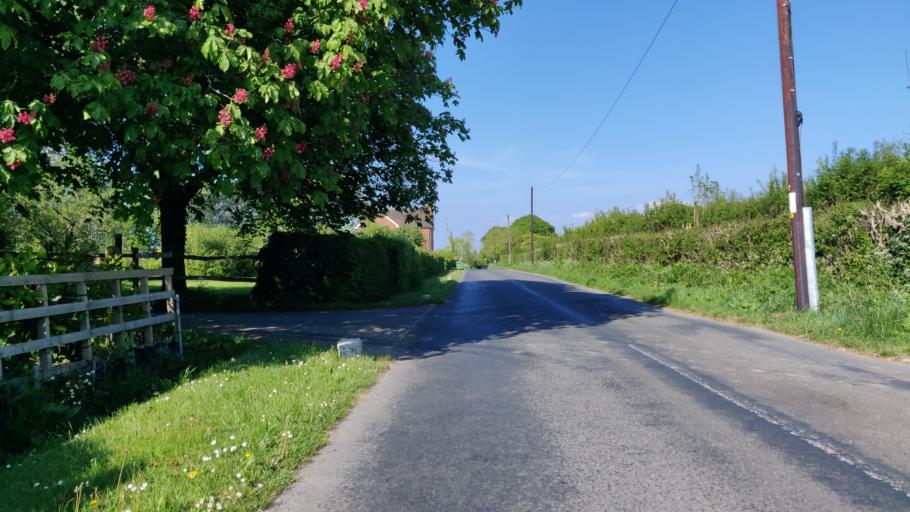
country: GB
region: England
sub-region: West Sussex
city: Southwater
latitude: 51.0291
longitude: -0.3732
